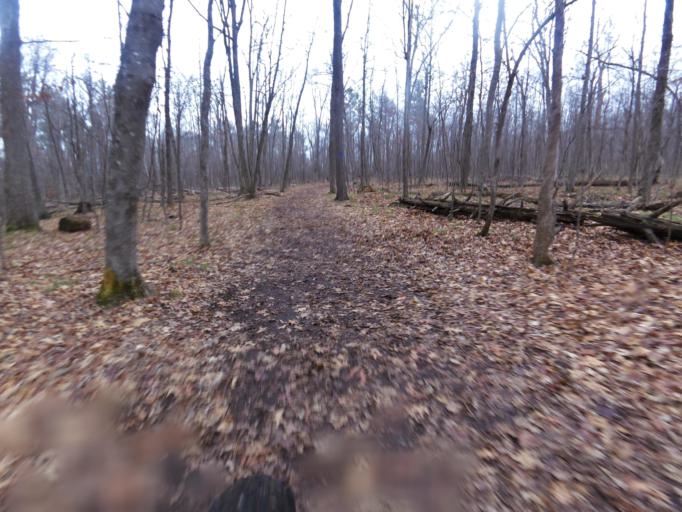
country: CA
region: Ontario
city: Bells Corners
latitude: 45.2901
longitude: -75.8108
